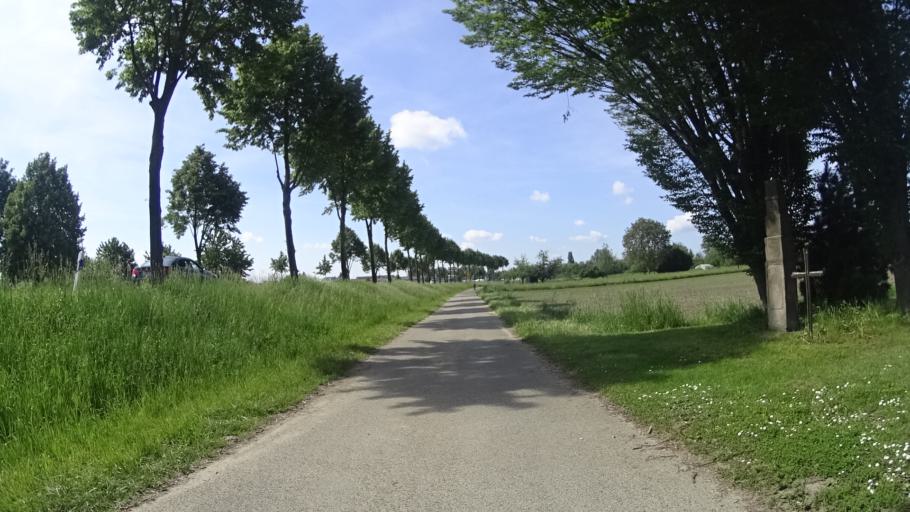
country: DE
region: Baden-Wuerttemberg
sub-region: Freiburg Region
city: Kehl
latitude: 48.5165
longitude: 7.8205
